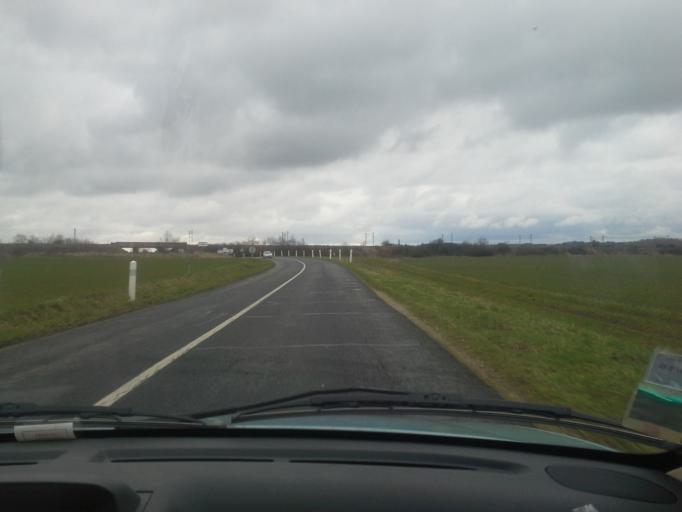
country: FR
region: Centre
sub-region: Departement du Loir-et-Cher
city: Villiers-sur-Loir
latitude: 47.7976
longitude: 1.0050
